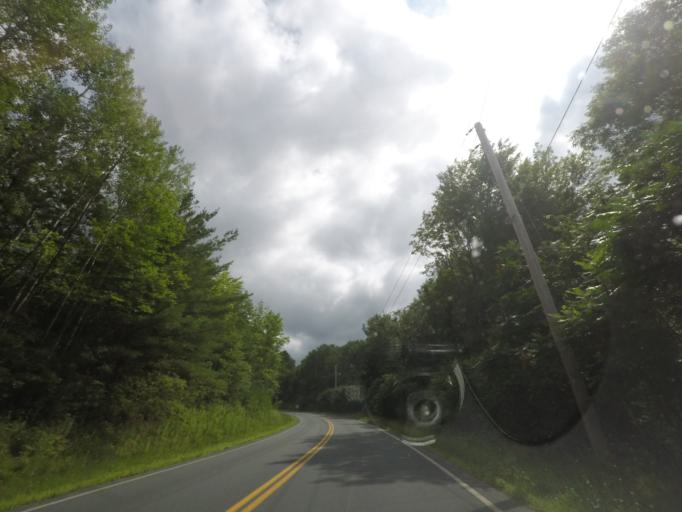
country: US
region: New York
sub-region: Saratoga County
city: Stillwater
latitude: 42.8852
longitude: -73.5623
